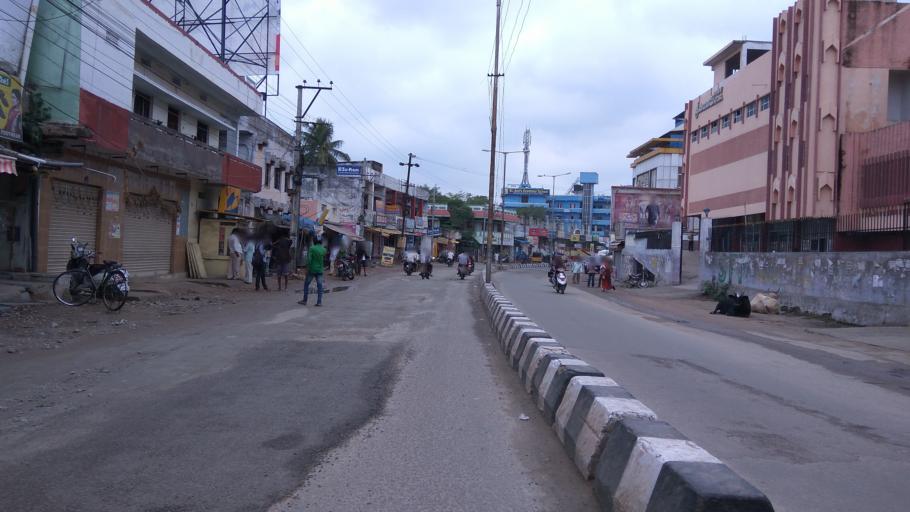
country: IN
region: Telangana
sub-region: Hyderabad
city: Malkajgiri
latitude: 17.4466
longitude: 78.5357
